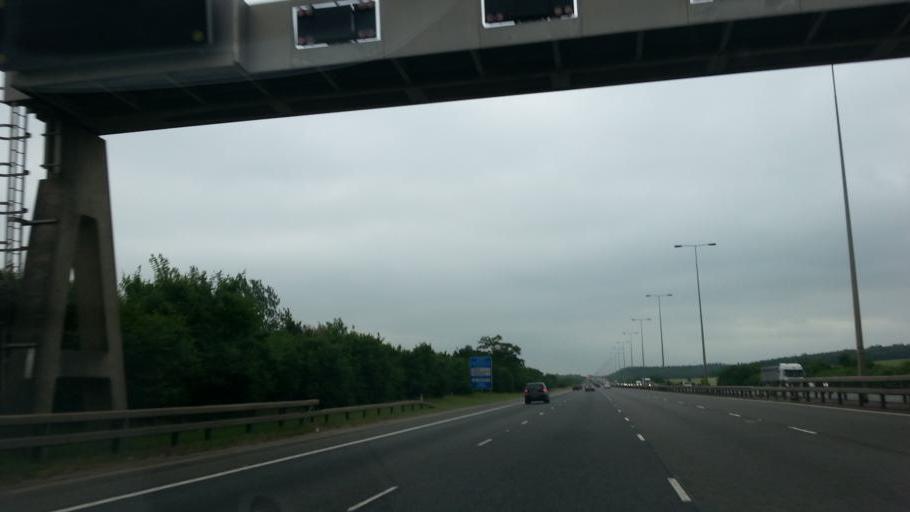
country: GB
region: England
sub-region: Cambridgeshire
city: Sawtry
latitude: 52.4178
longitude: -0.2674
